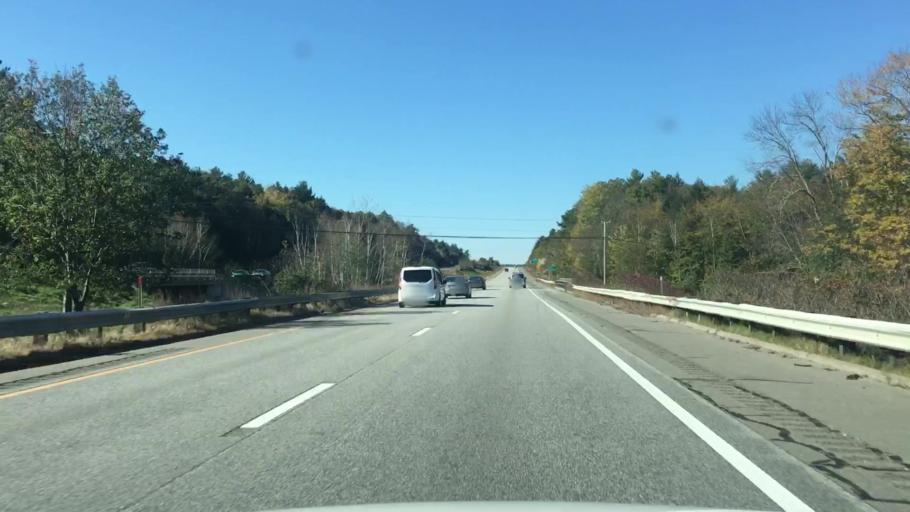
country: US
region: New Hampshire
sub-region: Rockingham County
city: Raymond
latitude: 43.0282
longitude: -71.1748
